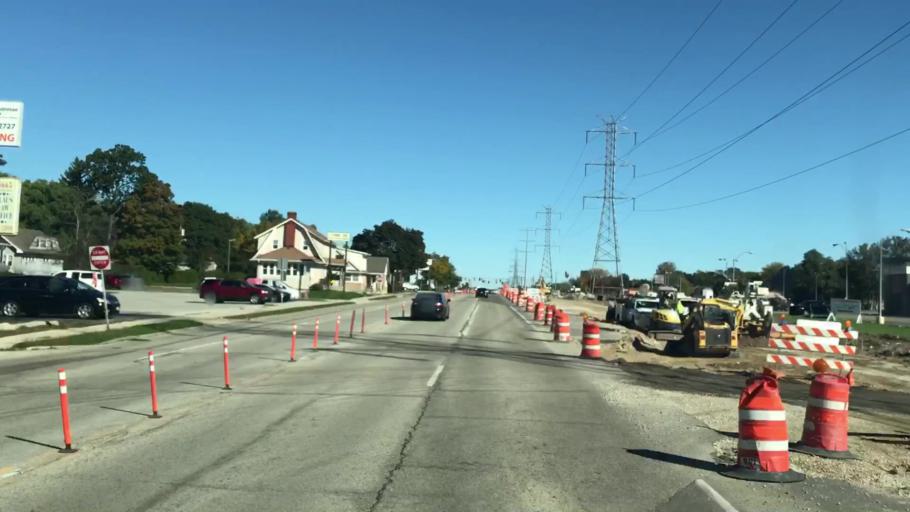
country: US
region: Wisconsin
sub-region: Milwaukee County
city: Hales Corners
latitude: 42.9409
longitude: -88.0485
